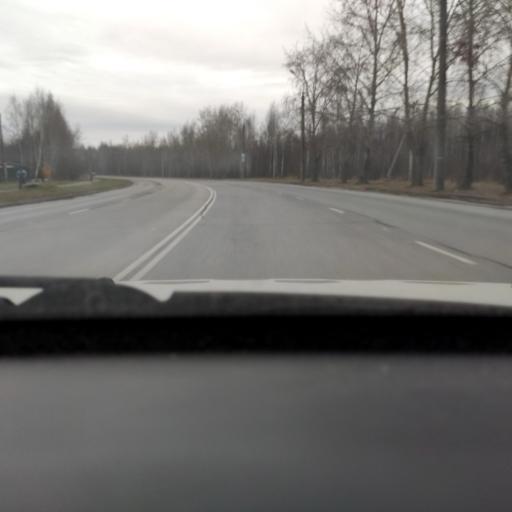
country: RU
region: Perm
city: Polazna
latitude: 58.1282
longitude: 56.4066
